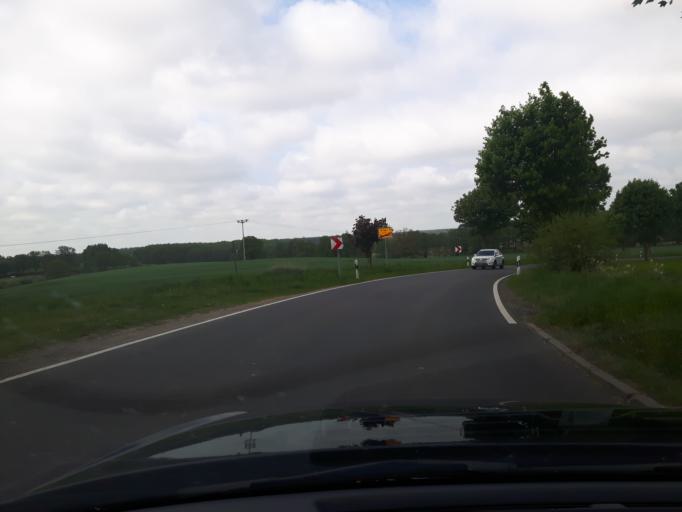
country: DE
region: Mecklenburg-Vorpommern
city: Grabowhofe
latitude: 53.5780
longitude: 12.5281
